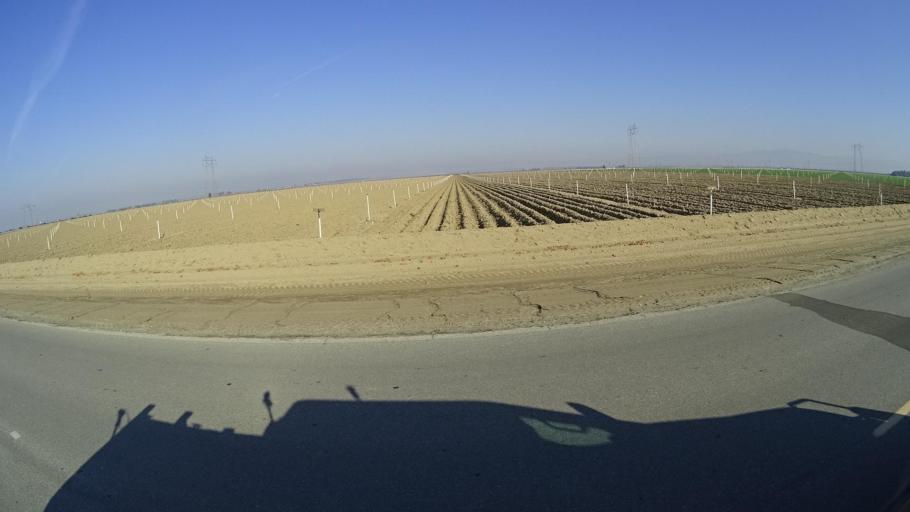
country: US
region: California
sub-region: Kern County
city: Weedpatch
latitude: 35.1219
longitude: -118.9834
